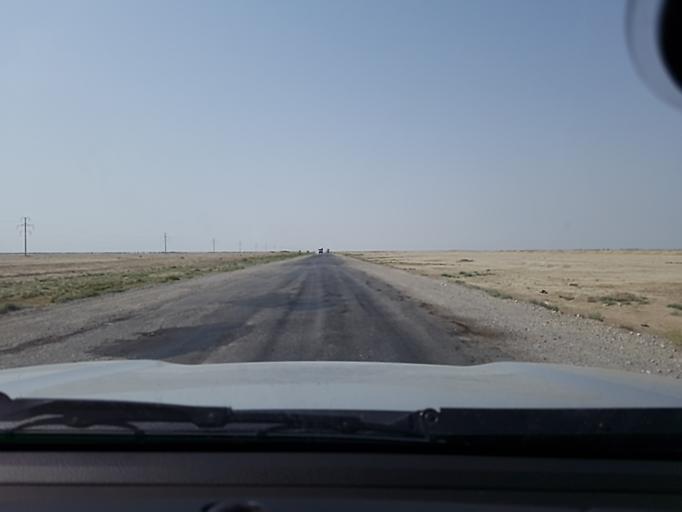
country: TM
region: Balkan
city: Gumdag
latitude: 38.8720
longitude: 54.5940
